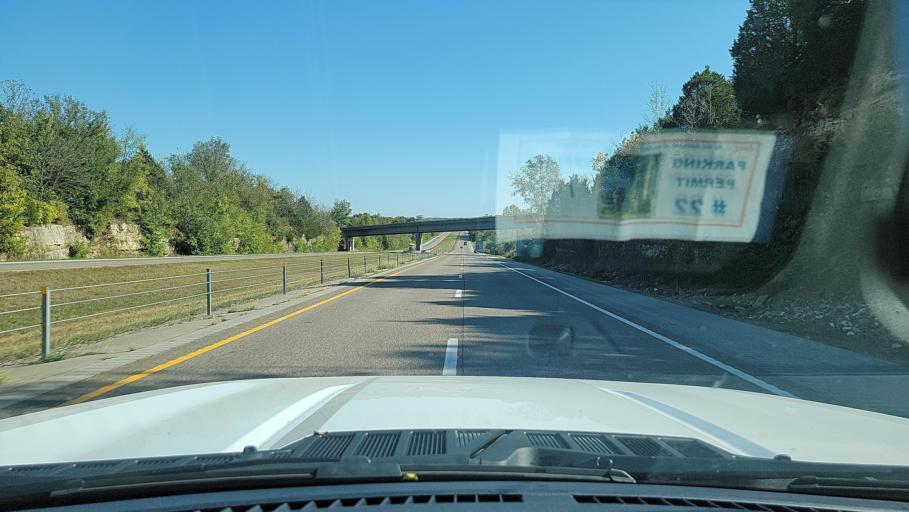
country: US
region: Missouri
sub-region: Jefferson County
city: Crystal City
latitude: 38.1398
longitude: -90.3302
